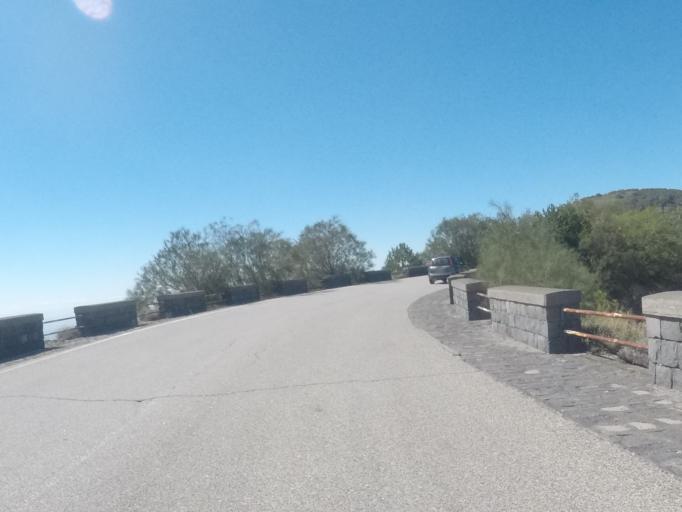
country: IT
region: Sicily
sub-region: Catania
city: Ragalna
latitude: 37.6757
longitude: 14.9797
